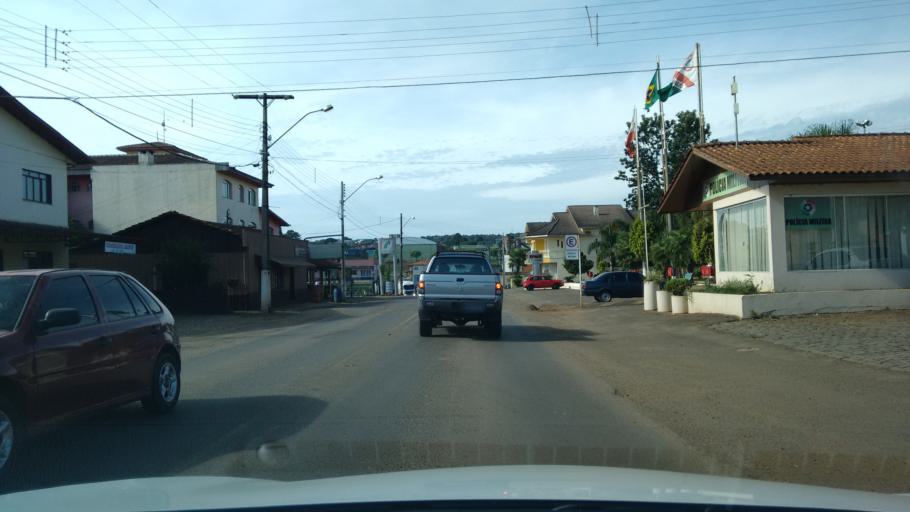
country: BR
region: Santa Catarina
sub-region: Videira
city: Videira
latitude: -27.2211
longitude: -50.9791
